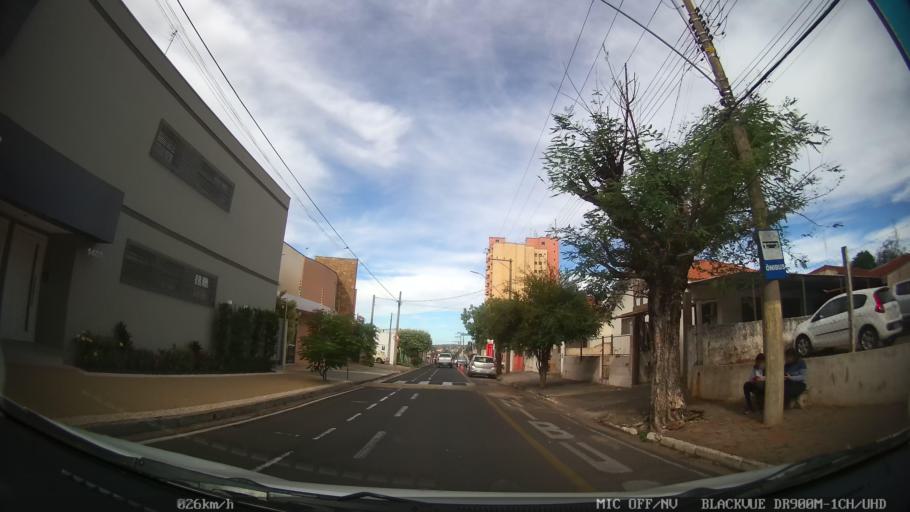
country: BR
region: Sao Paulo
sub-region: Catanduva
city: Catanduva
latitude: -21.1428
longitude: -48.9761
